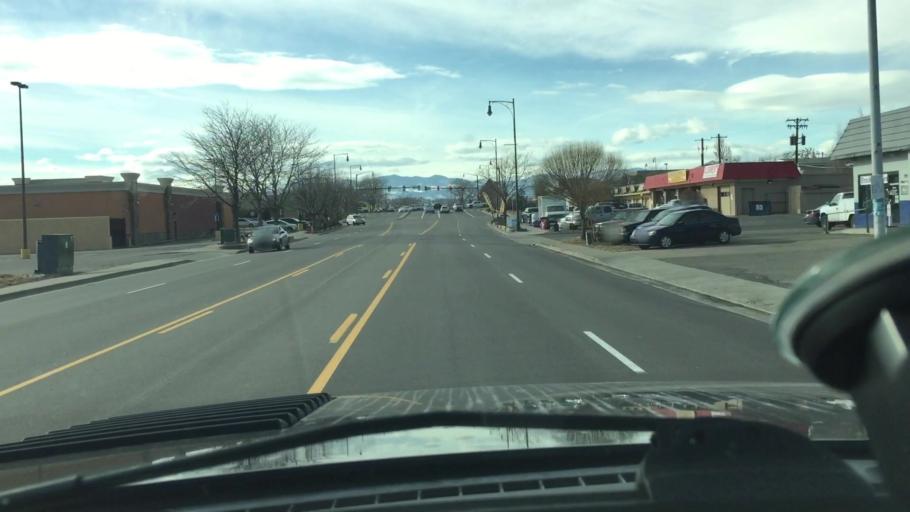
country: US
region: Colorado
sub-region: Adams County
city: Twin Lakes
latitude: 39.8273
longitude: -105.0221
